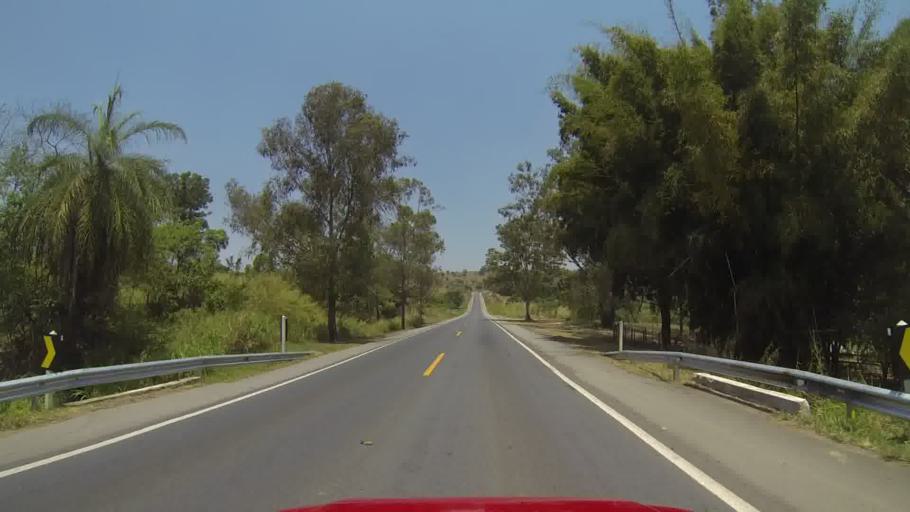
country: BR
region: Minas Gerais
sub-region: Itapecerica
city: Itapecerica
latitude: -20.3341
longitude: -45.2313
